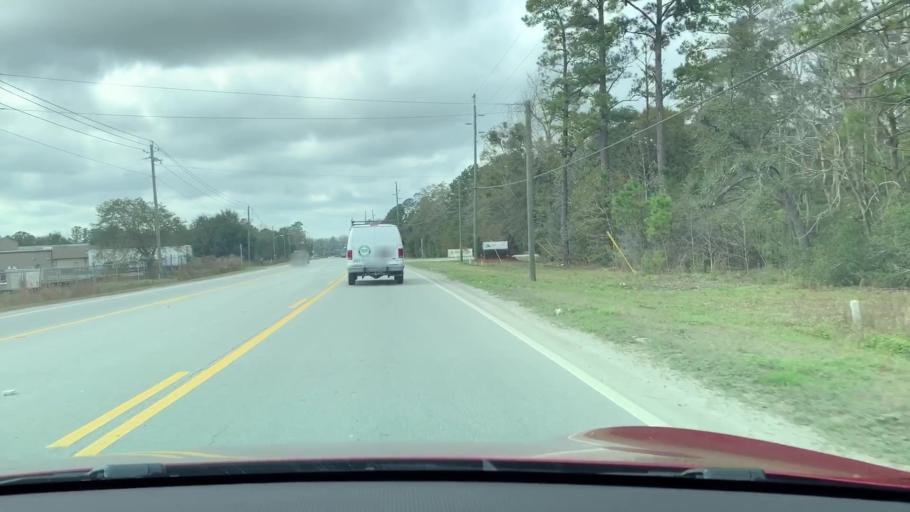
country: US
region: Georgia
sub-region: Chatham County
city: Port Wentworth
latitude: 32.1449
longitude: -81.1848
